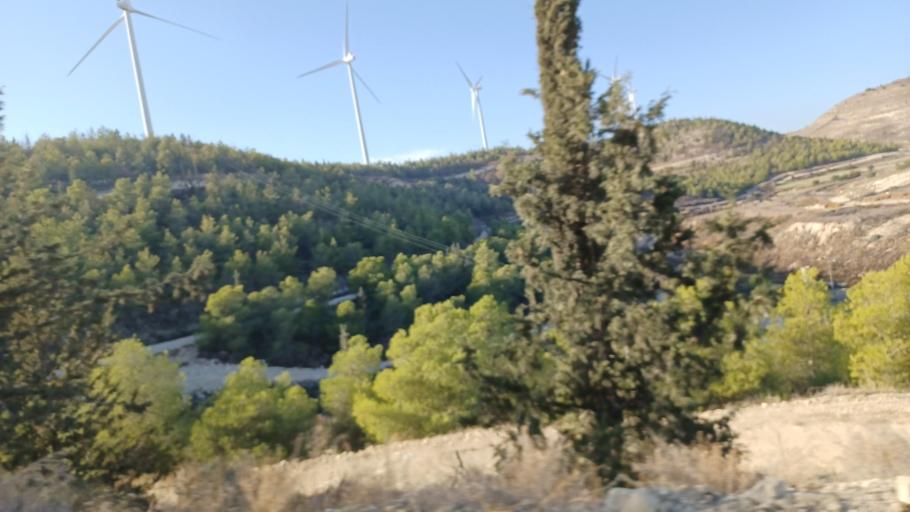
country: CY
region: Larnaka
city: Psevdas
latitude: 34.9608
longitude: 33.5145
